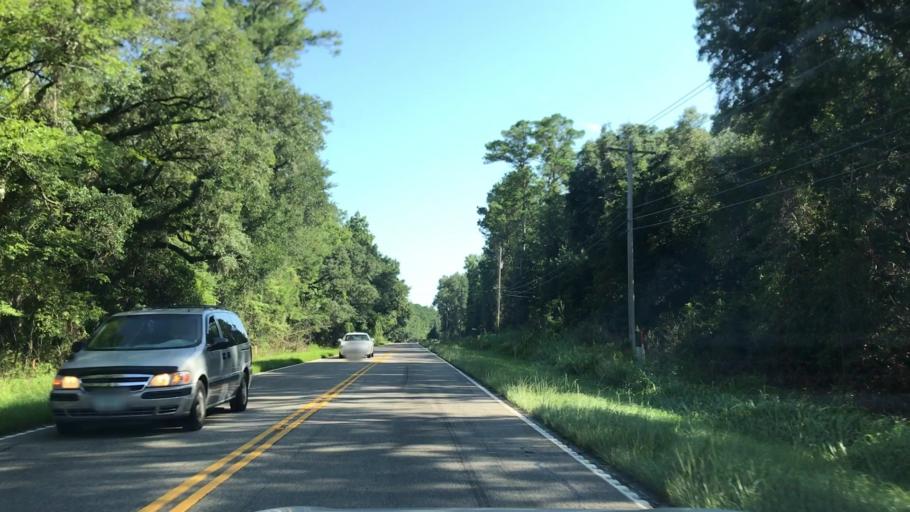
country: US
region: South Carolina
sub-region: Georgetown County
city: Georgetown
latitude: 33.4708
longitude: -79.2793
